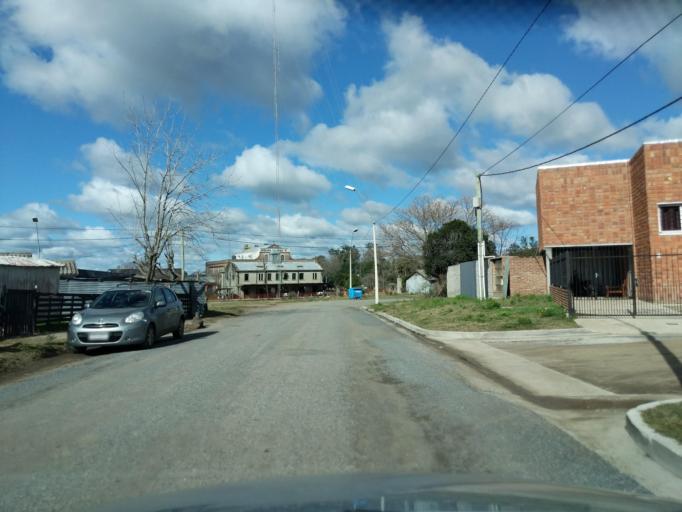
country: UY
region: Florida
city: Florida
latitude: -34.0967
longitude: -56.2333
